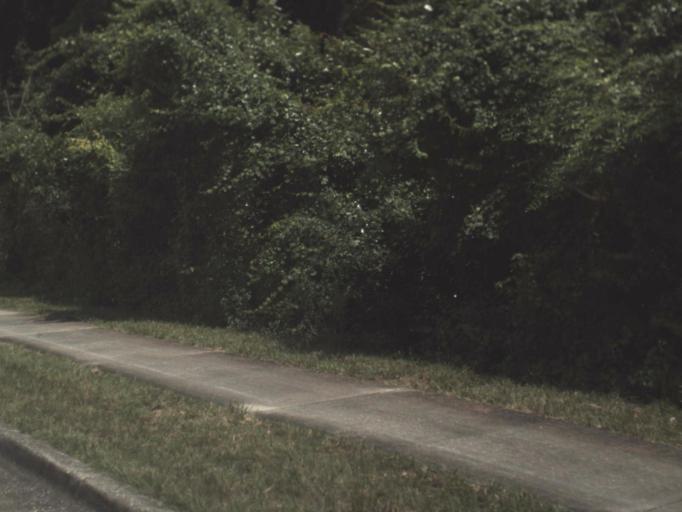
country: US
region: Florida
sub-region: Columbia County
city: Watertown
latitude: 30.1831
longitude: -82.6224
